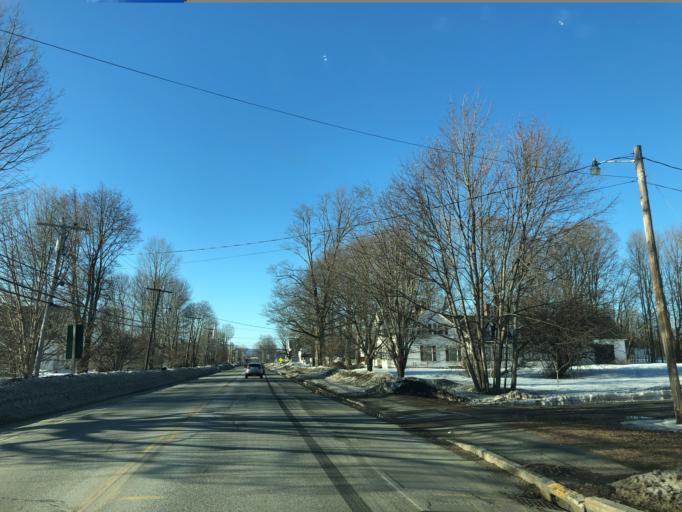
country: US
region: Maine
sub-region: Penobscot County
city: Charleston
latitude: 44.9991
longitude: -69.0213
